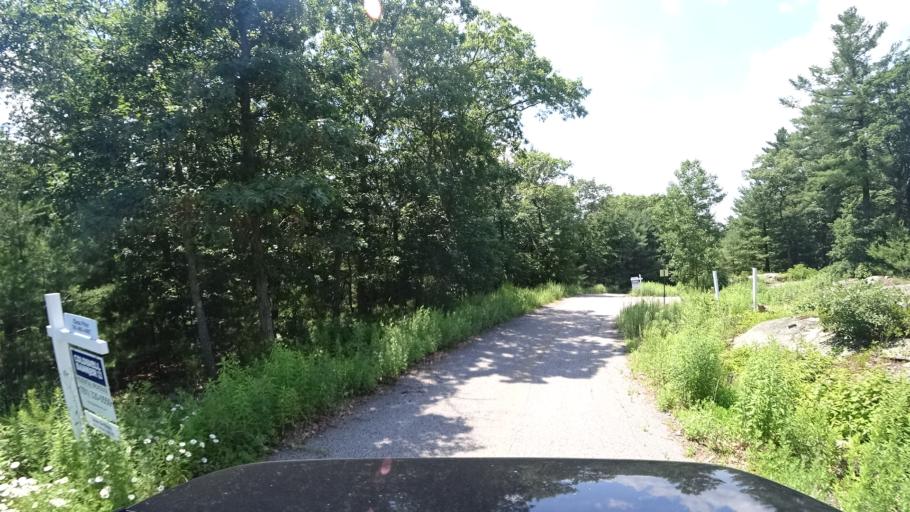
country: US
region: Massachusetts
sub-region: Norfolk County
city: Dedham
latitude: 42.2469
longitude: -71.1999
